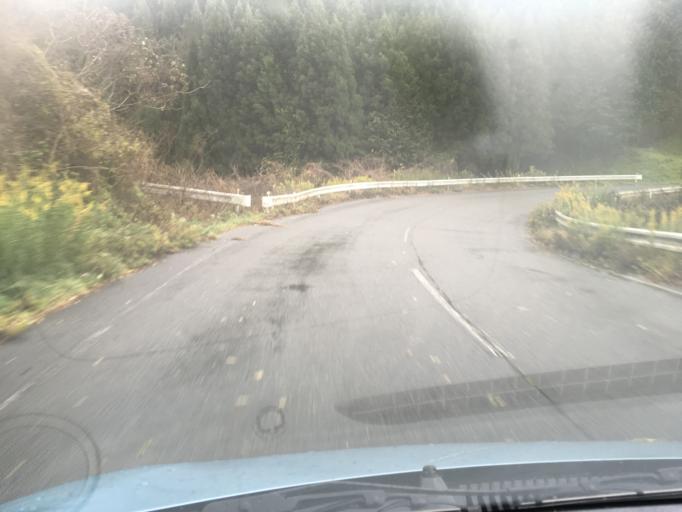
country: JP
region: Iwate
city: Ichinoseki
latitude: 38.8287
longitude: 141.2580
